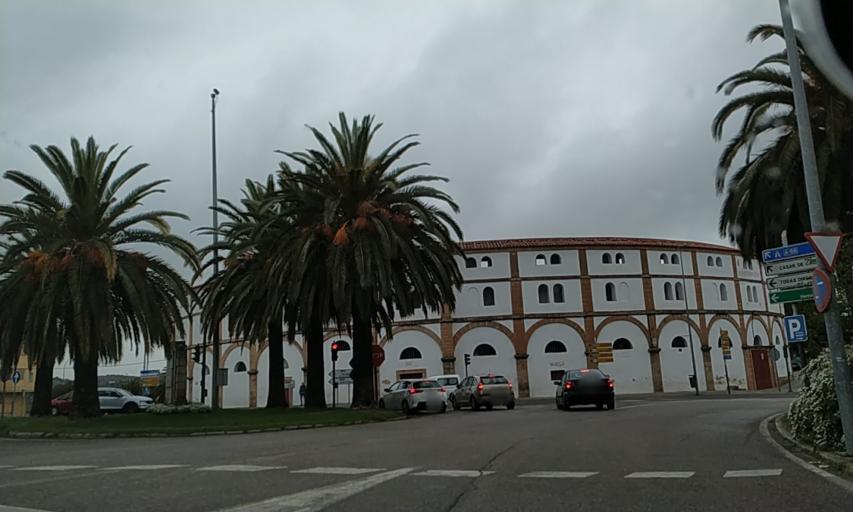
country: ES
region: Extremadura
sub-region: Provincia de Caceres
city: Caceres
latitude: 39.4797
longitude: -6.3750
